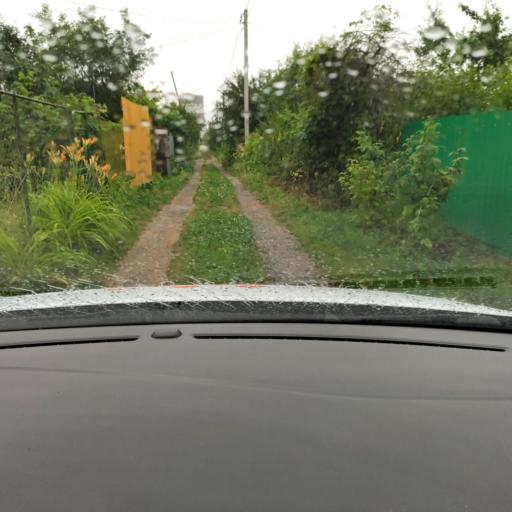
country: RU
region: Tatarstan
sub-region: Gorod Kazan'
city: Kazan
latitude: 55.8528
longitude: 49.0578
